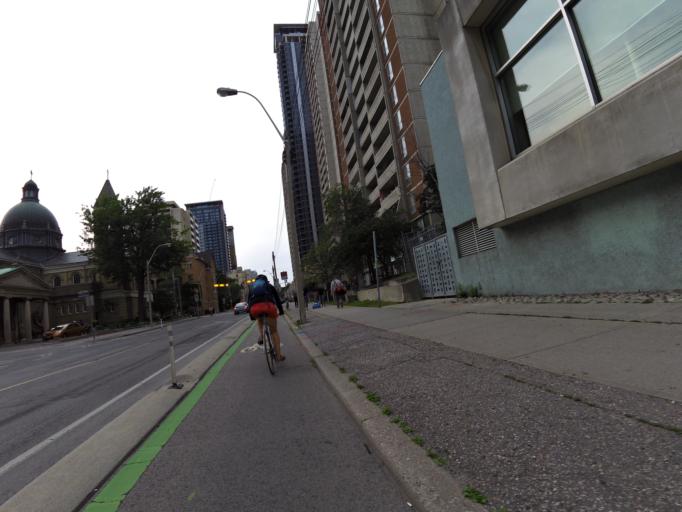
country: CA
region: Ontario
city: Toronto
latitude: 43.6681
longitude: -79.3750
